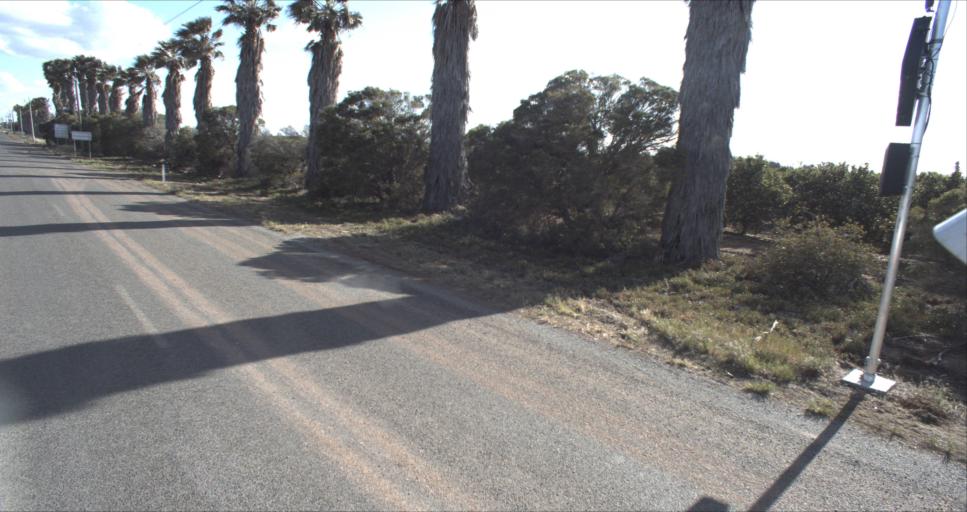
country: AU
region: New South Wales
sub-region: Leeton
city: Leeton
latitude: -34.5217
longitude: 146.2831
